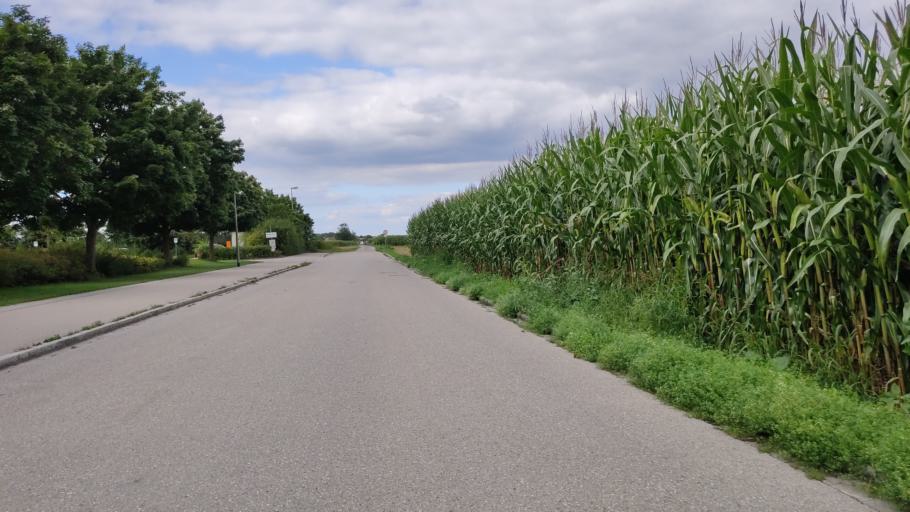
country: DE
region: Bavaria
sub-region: Swabia
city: Konigsbrunn
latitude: 48.2588
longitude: 10.8748
